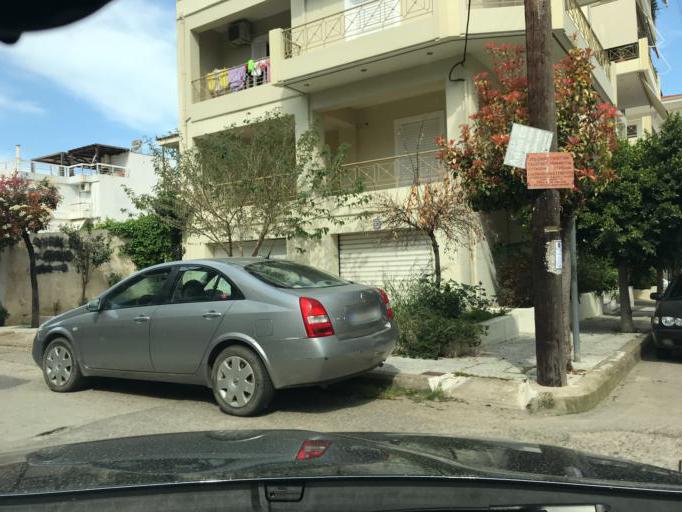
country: GR
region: West Greece
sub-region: Nomos Ileias
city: Pyrgos
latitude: 37.6750
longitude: 21.4402
